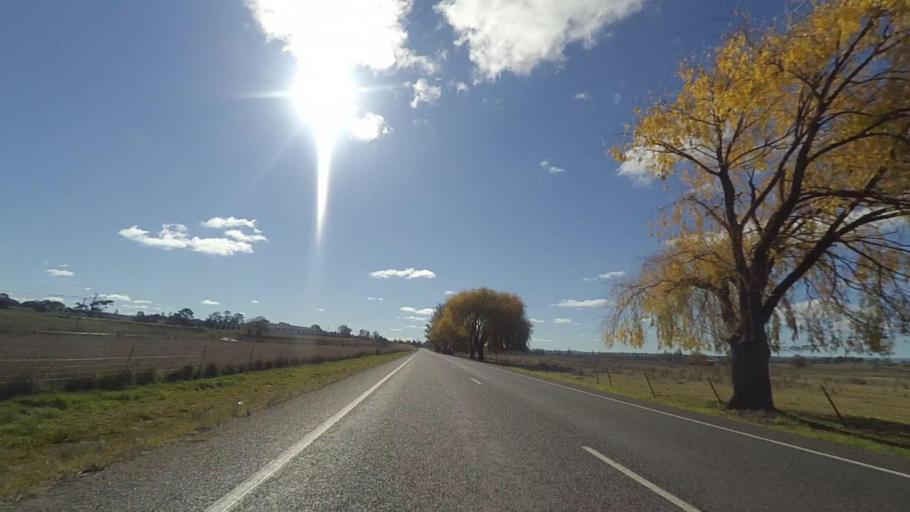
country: AU
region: New South Wales
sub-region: Bathurst Regional
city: Bathurst
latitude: -33.4473
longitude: 149.5789
